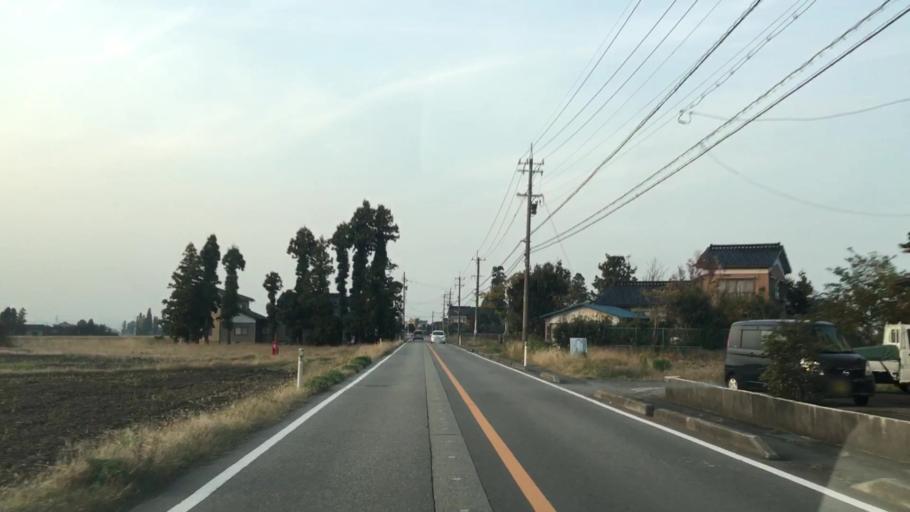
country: JP
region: Toyama
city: Toyama-shi
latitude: 36.6075
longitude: 137.2529
